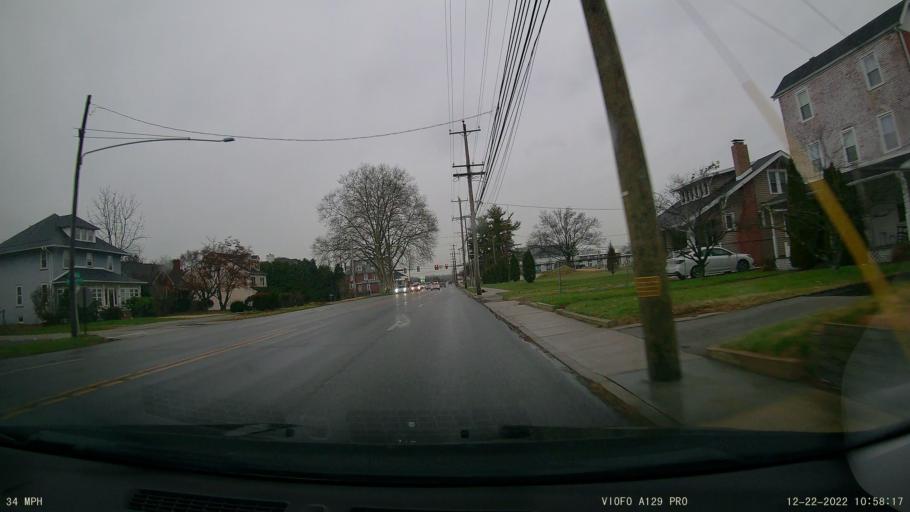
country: US
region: Pennsylvania
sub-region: Montgomery County
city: West Norriton
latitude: 40.1301
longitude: -75.3738
